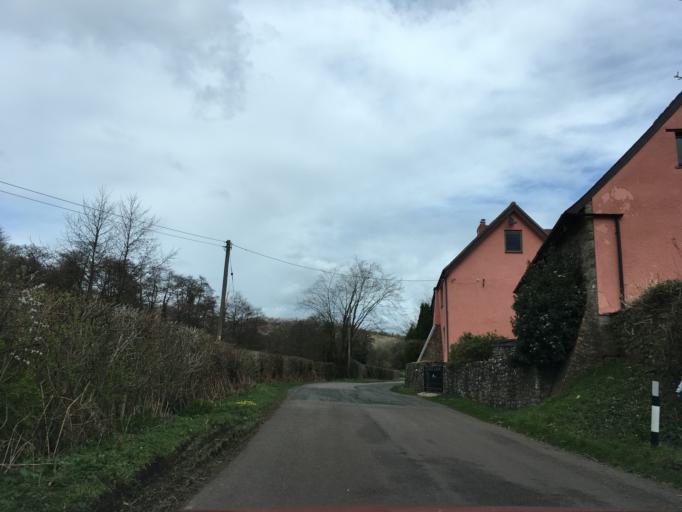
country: GB
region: England
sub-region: Gloucestershire
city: Coleford
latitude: 51.7796
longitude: -2.6326
